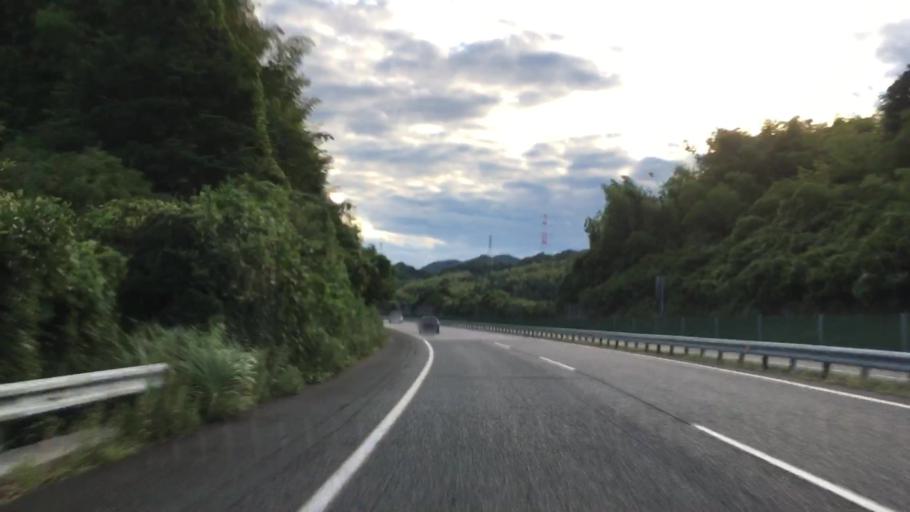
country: JP
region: Yamaguchi
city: Shimonoseki
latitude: 34.0449
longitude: 130.9905
